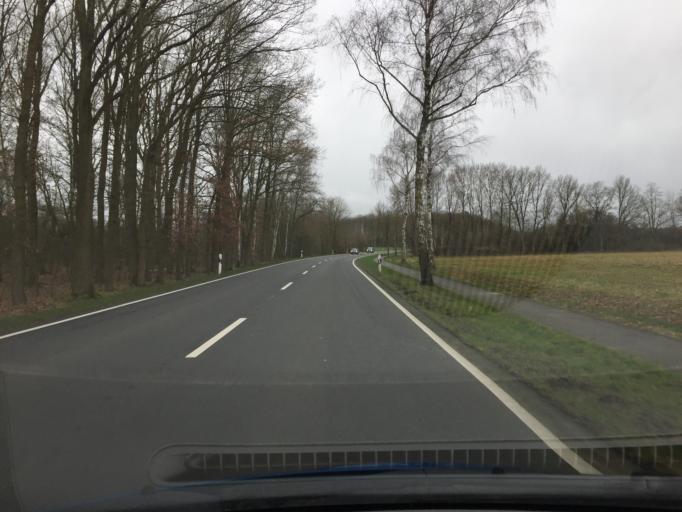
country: DE
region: Lower Saxony
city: Ratzlingen
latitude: 52.9863
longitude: 10.6327
